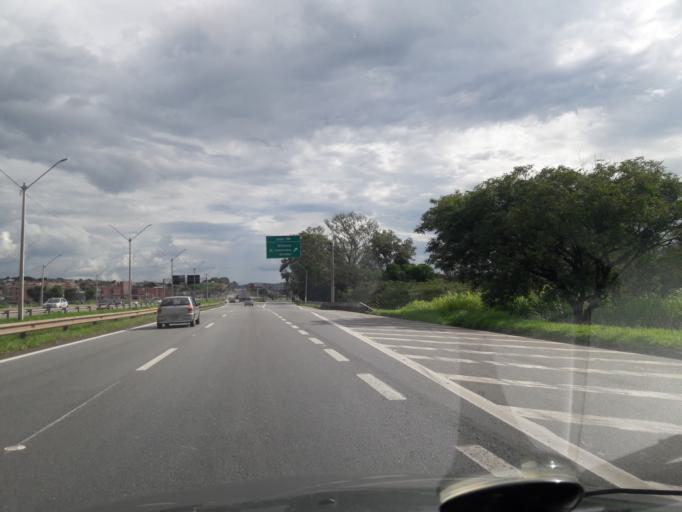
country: BR
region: Sao Paulo
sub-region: Atibaia
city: Atibaia
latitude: -23.1094
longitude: -46.5704
